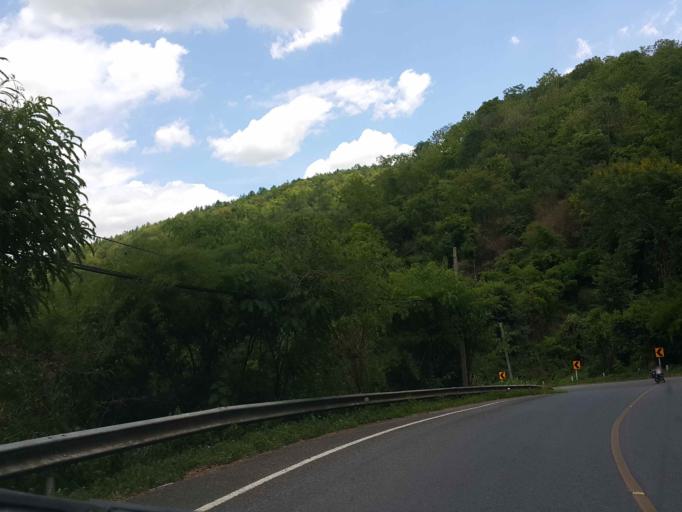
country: TH
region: Chiang Mai
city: Hang Dong
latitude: 18.7567
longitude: 98.8809
